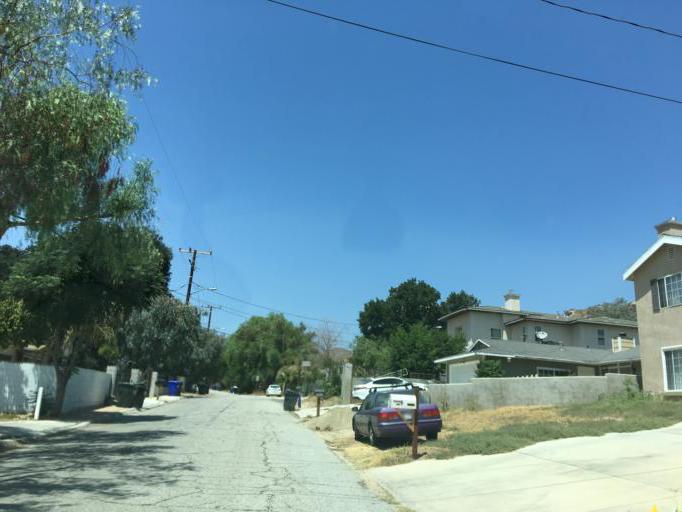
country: US
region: California
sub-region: Los Angeles County
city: Val Verde
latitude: 34.4479
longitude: -118.6663
